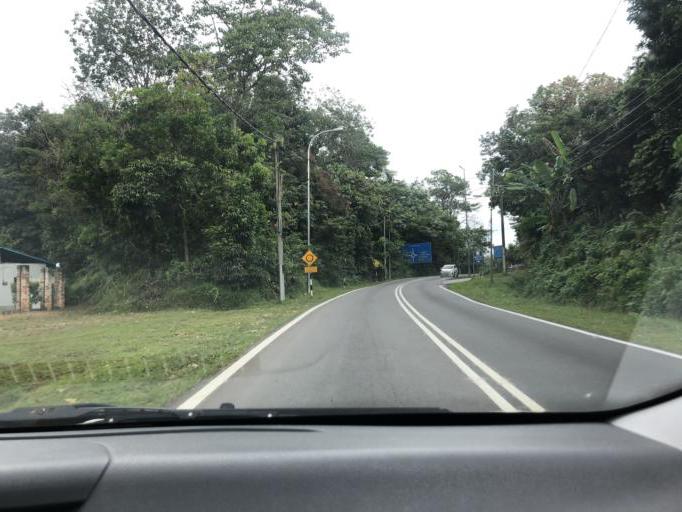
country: MY
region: Putrajaya
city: Putrajaya
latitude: 2.9206
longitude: 101.7484
